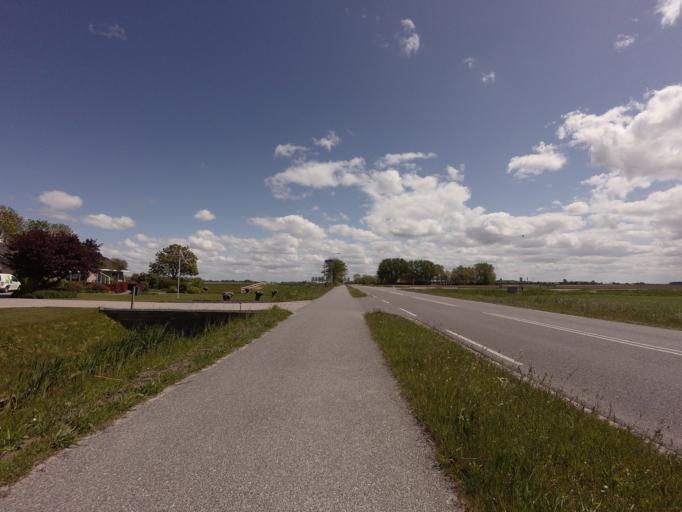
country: NL
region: Friesland
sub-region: Gemeente Harlingen
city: Harlingen
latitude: 53.1364
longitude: 5.4605
